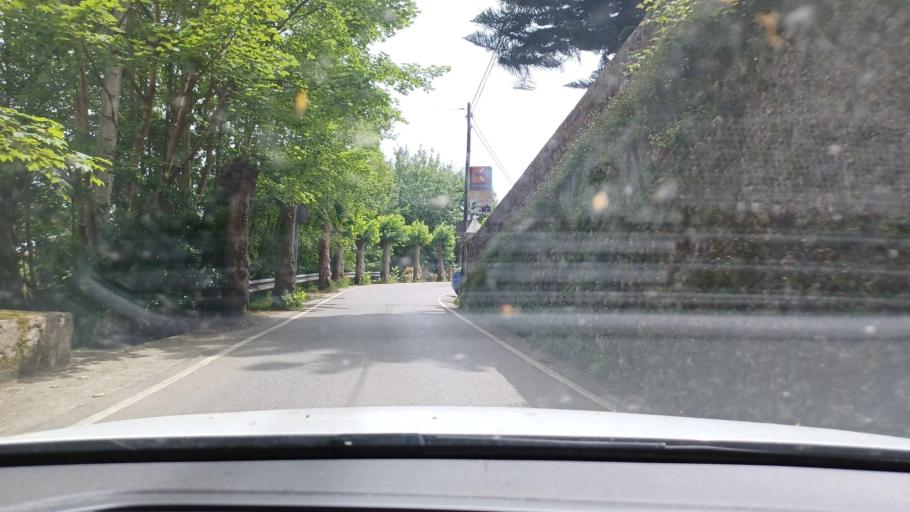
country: ES
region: Asturias
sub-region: Province of Asturias
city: Llanes
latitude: 43.4185
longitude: -4.7570
